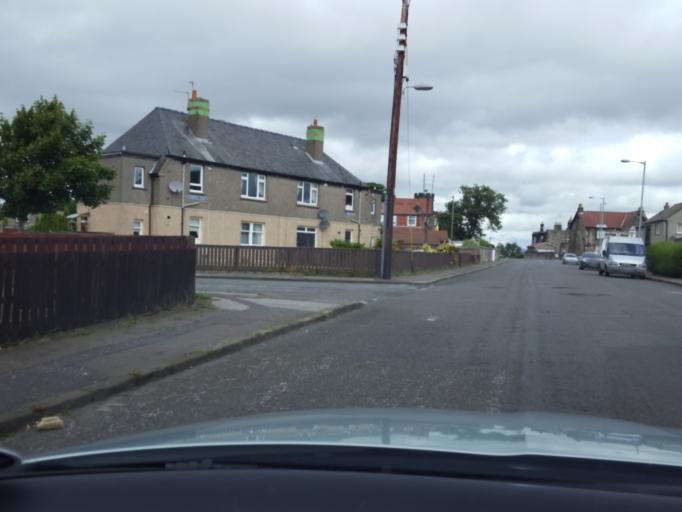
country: GB
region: Scotland
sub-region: Falkirk
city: Bo'ness
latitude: 56.0109
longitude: -3.6060
